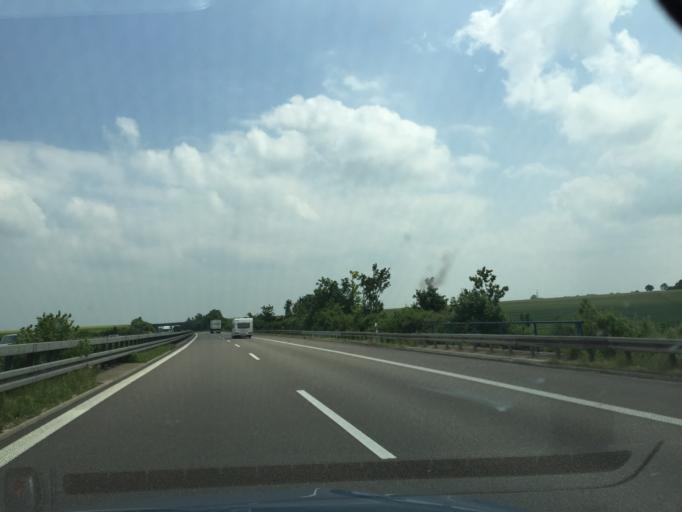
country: DE
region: Baden-Wuerttemberg
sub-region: Tuebingen Region
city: Langenau
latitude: 48.4883
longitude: 10.0930
